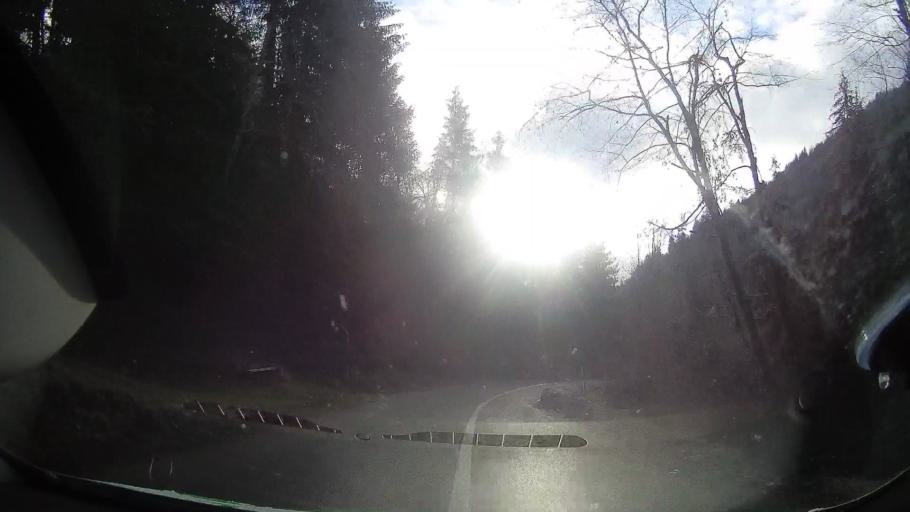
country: RO
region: Alba
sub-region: Comuna Albac
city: Albac
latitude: 46.4750
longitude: 22.9627
